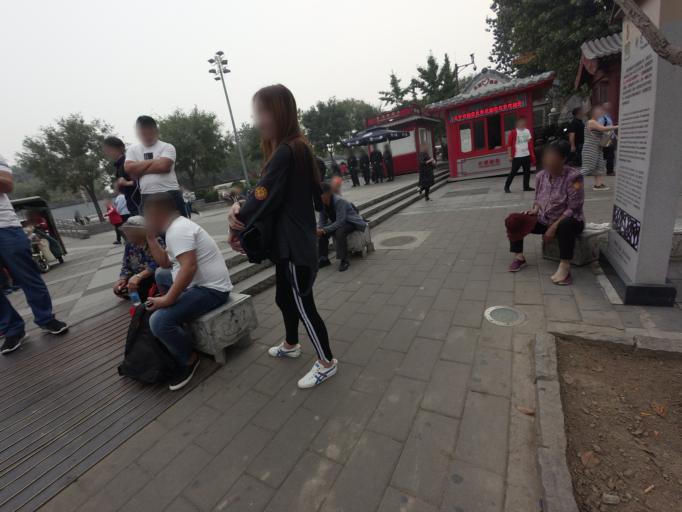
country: CN
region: Beijing
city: Jingshan
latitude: 39.9325
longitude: 116.3859
